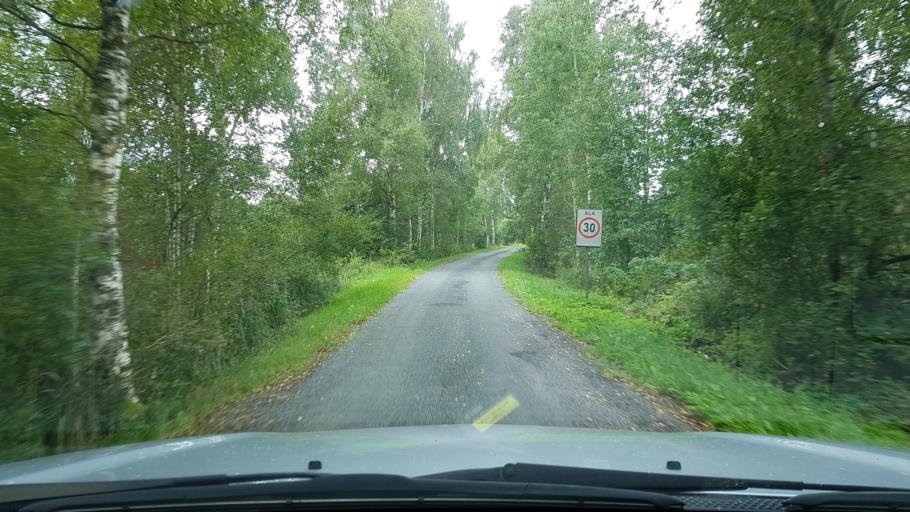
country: EE
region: Harju
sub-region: Raasiku vald
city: Arukula
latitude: 59.2913
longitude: 25.0777
